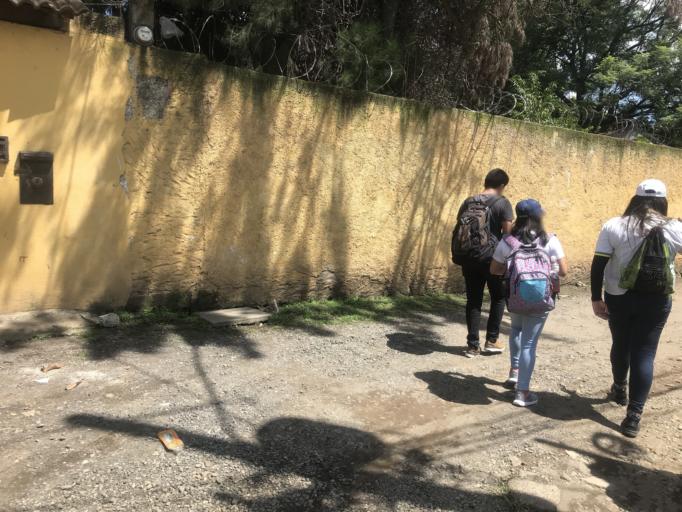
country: GT
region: Guatemala
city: Amatitlan
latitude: 14.4805
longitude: -90.6353
